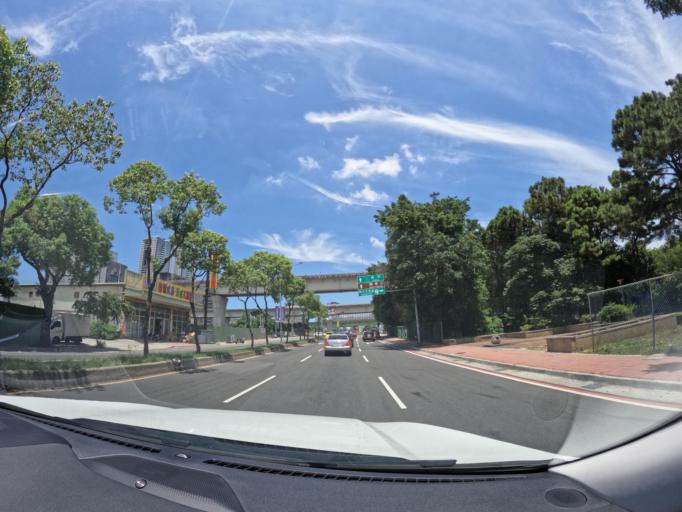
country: TW
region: Taiwan
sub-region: Taoyuan
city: Taoyuan
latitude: 25.0632
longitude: 121.3649
